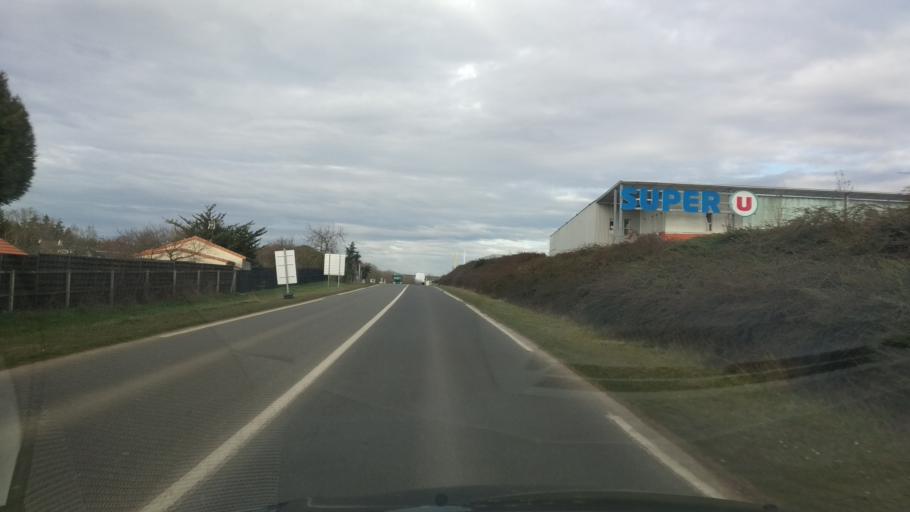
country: FR
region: Poitou-Charentes
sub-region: Departement de la Vienne
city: Saint-Georges-les-Baillargeaux
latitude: 46.6689
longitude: 0.4046
